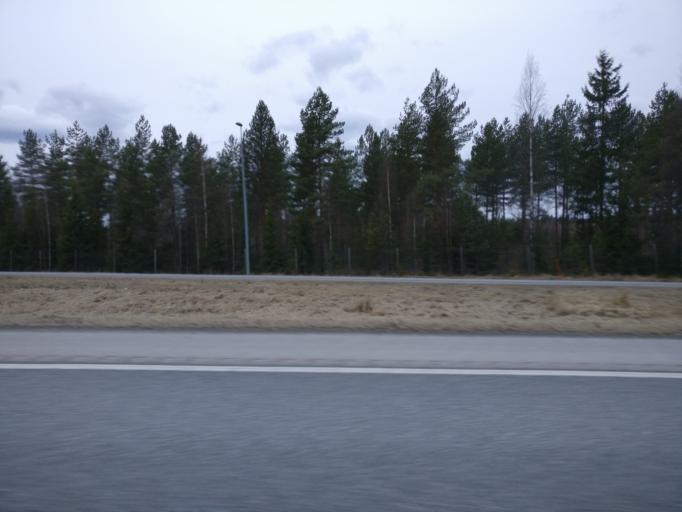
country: FI
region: Haeme
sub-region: Riihimaeki
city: Riihimaeki
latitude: 60.7545
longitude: 24.7291
